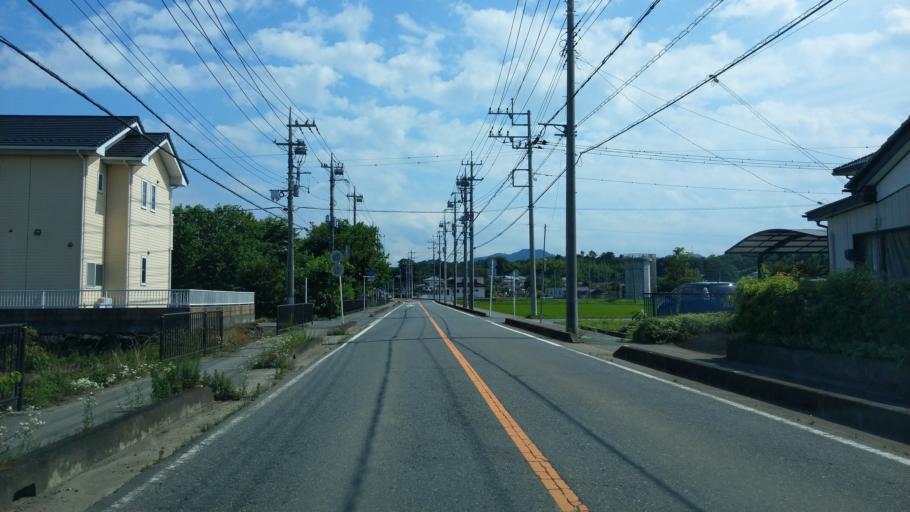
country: JP
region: Saitama
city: Kodamacho-kodamaminami
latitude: 36.2071
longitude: 139.1518
